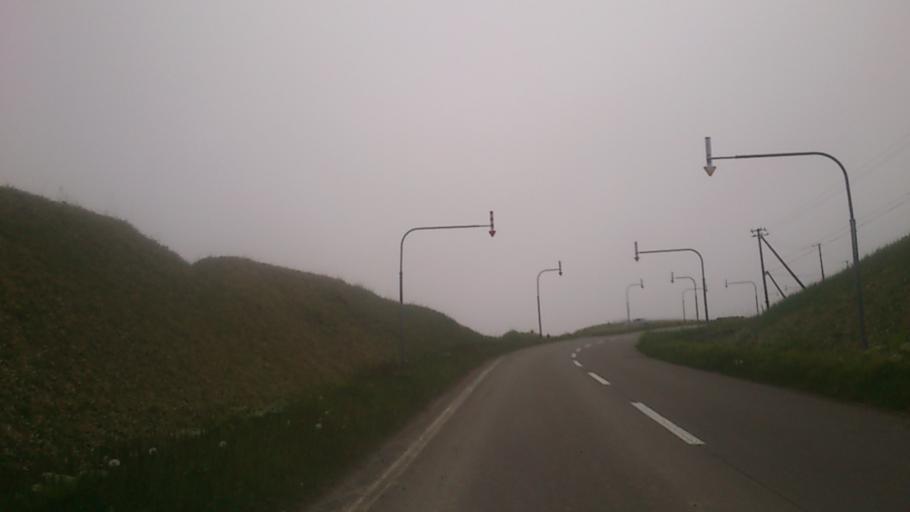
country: JP
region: Hokkaido
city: Nemuro
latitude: 43.1740
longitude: 145.2958
